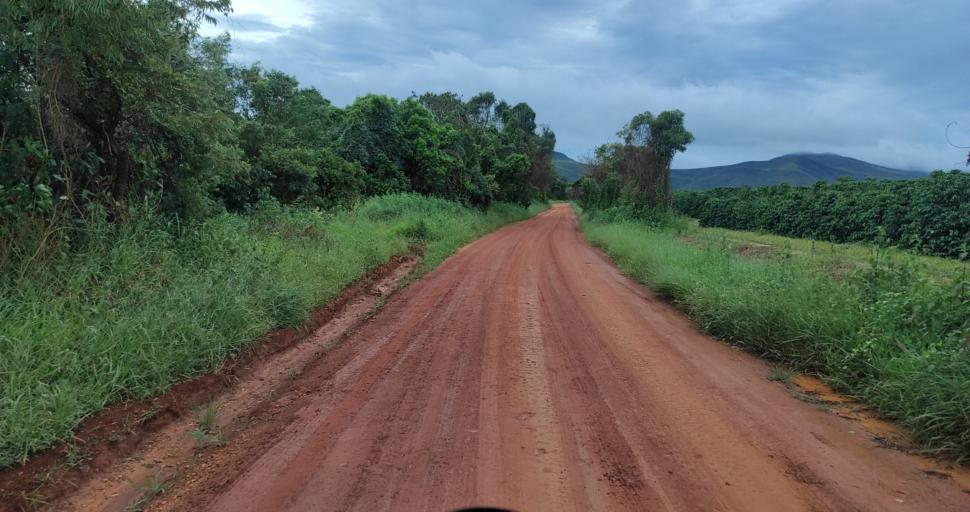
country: BR
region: Minas Gerais
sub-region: Piui
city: Piui
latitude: -20.2810
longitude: -46.3615
